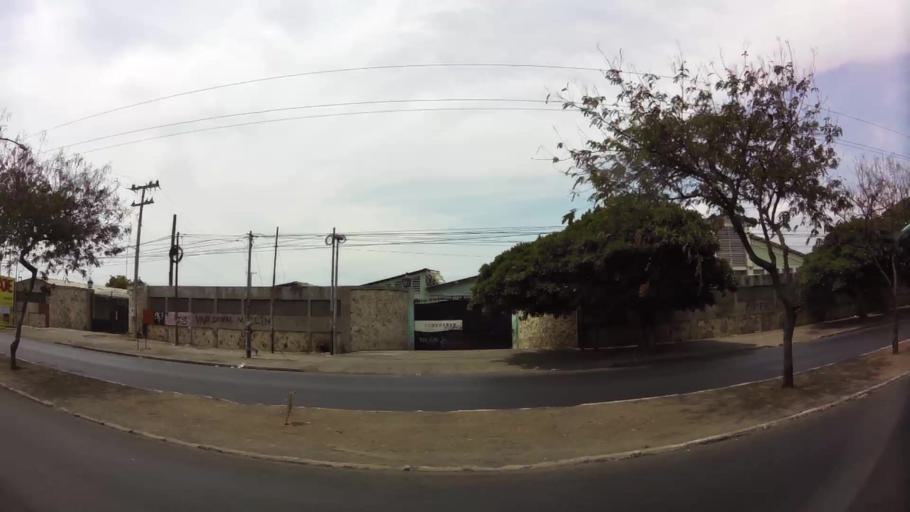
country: NI
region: Managua
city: Managua
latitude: 12.1520
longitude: -86.2401
